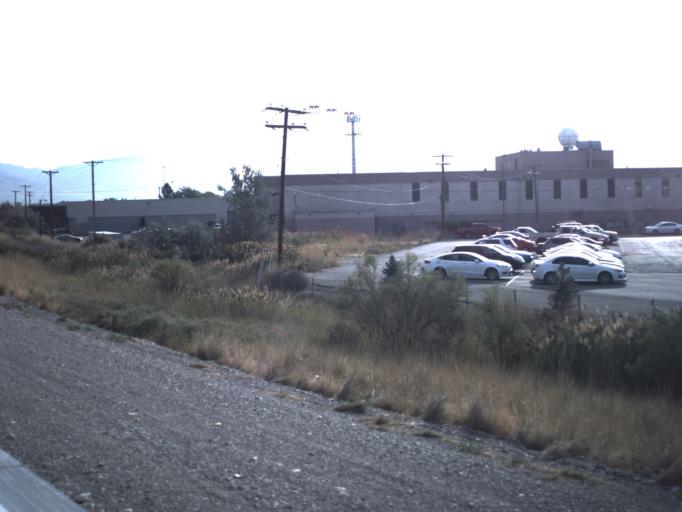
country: US
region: Utah
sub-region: Salt Lake County
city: Taylorsville
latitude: 40.7223
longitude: -111.9514
